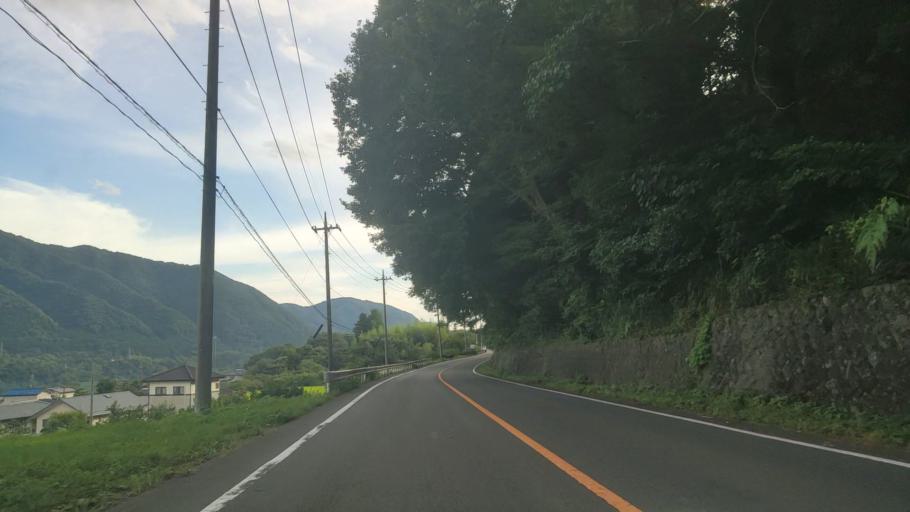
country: JP
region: Gunma
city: Omamacho-omama
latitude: 36.5268
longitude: 139.3128
